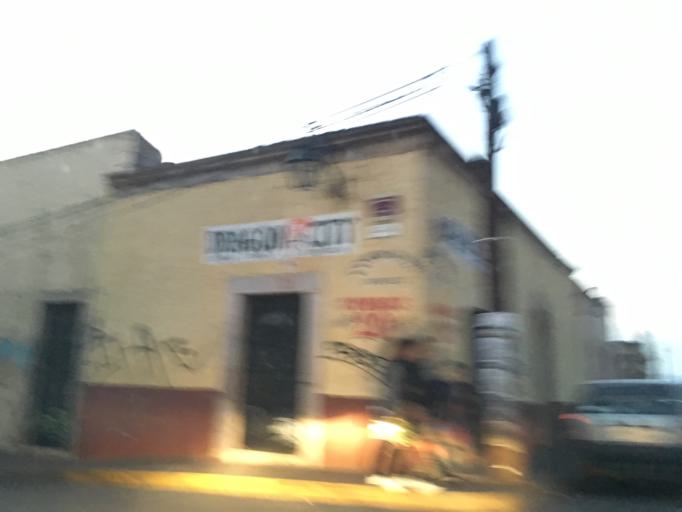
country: MX
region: Michoacan
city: Morelia
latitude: 19.7056
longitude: -101.1922
